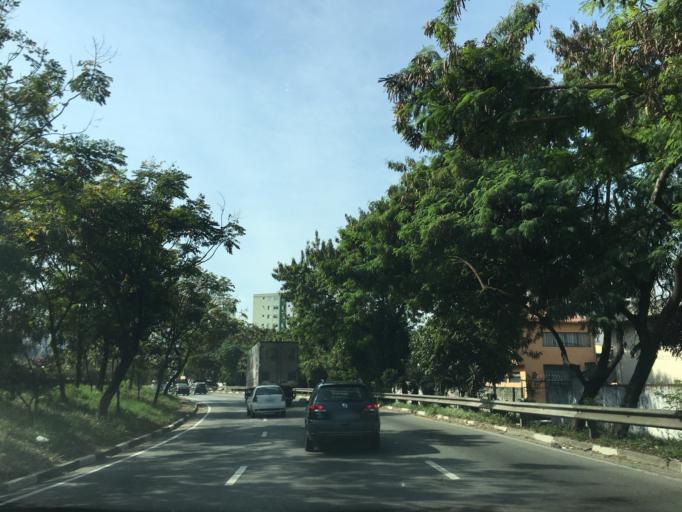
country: BR
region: Sao Paulo
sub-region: Osasco
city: Osasco
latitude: -23.5629
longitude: -46.7496
